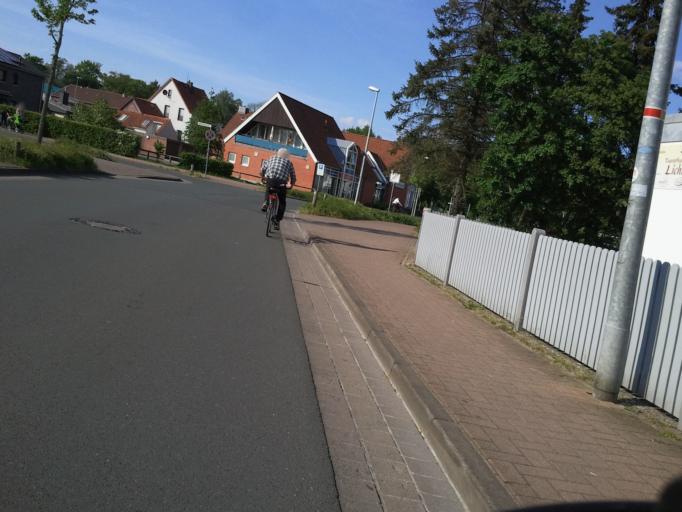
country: DE
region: Lower Saxony
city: Nienburg
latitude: 52.6281
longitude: 9.2200
